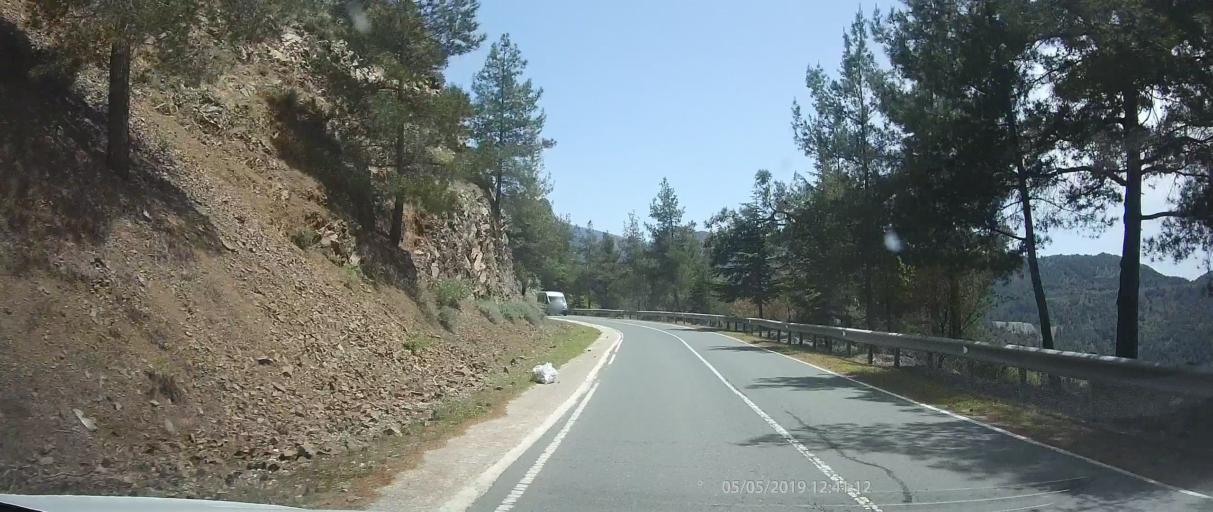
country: CY
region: Lefkosia
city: Kakopetria
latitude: 34.9841
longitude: 32.8064
